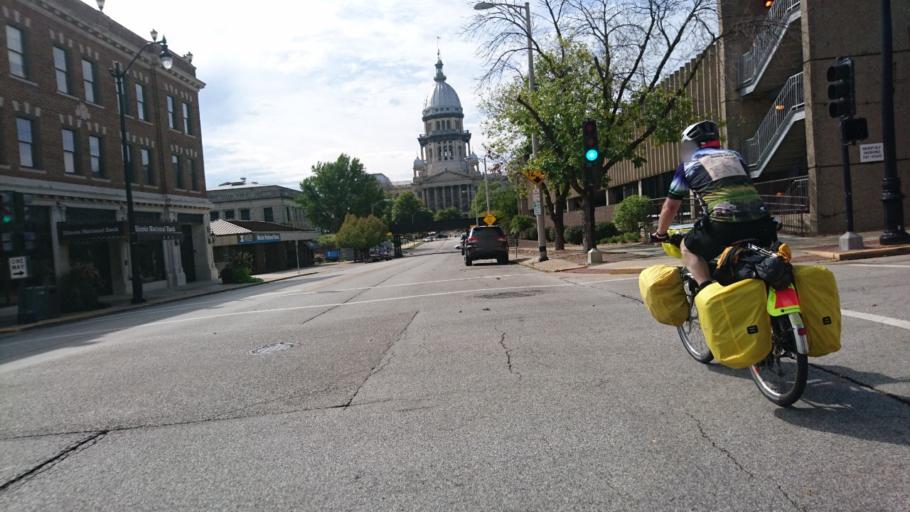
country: US
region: Illinois
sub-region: Sangamon County
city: Springfield
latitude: 39.7985
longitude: -89.6507
